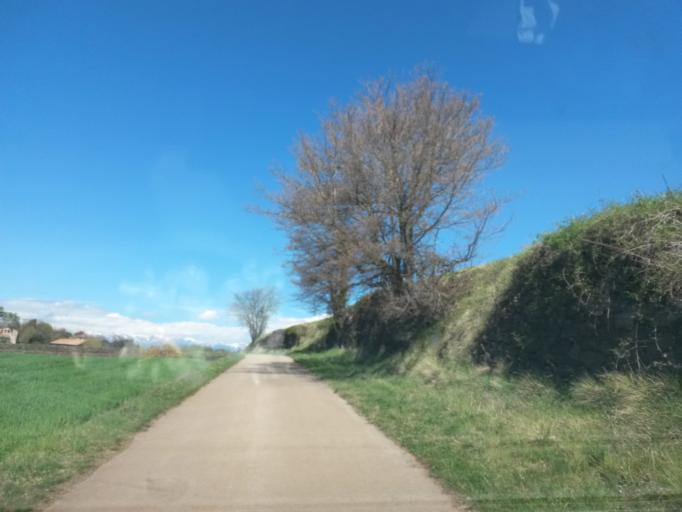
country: ES
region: Catalonia
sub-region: Provincia de Girona
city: Sant Cristofol de les Fonts
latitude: 42.1700
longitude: 2.5331
